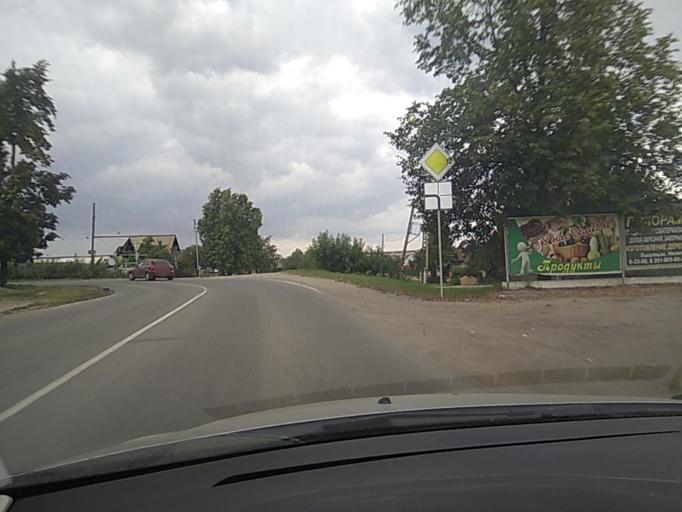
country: RU
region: Chelyabinsk
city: Kyshtym
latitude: 55.7093
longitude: 60.5190
